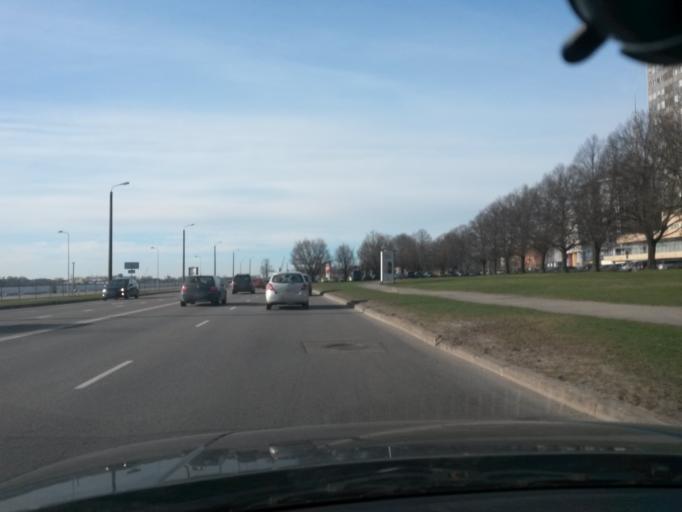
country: LV
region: Riga
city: Riga
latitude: 56.9530
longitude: 24.0983
